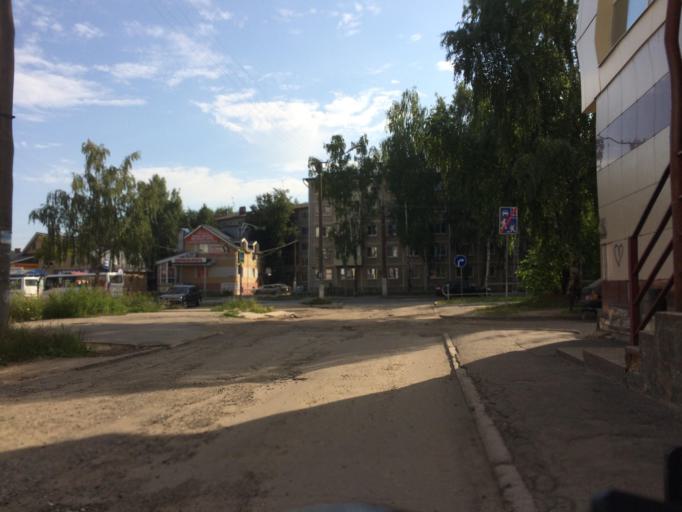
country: RU
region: Mariy-El
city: Medvedevo
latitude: 56.6382
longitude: 47.8322
